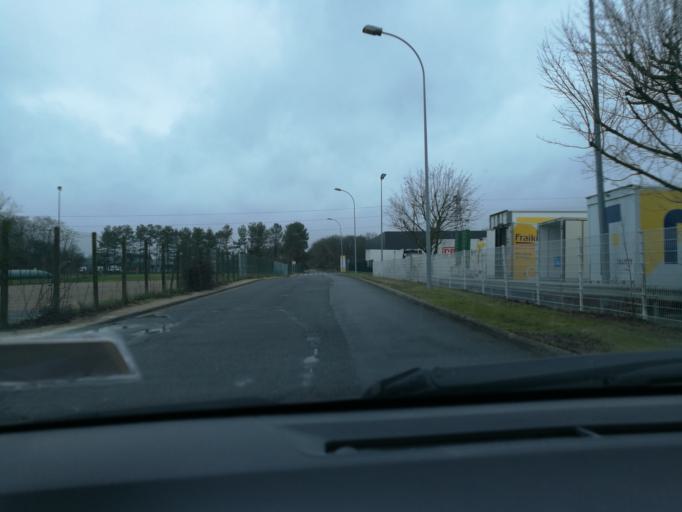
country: FR
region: Centre
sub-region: Departement du Loiret
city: Fleury-les-Aubrais
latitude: 47.9446
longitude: 1.9276
